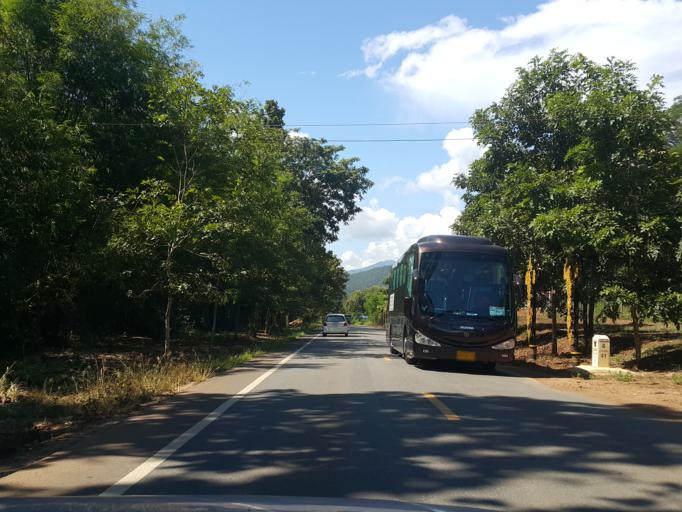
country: TH
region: Chiang Mai
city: Mae Taeng
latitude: 19.1667
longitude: 98.9310
